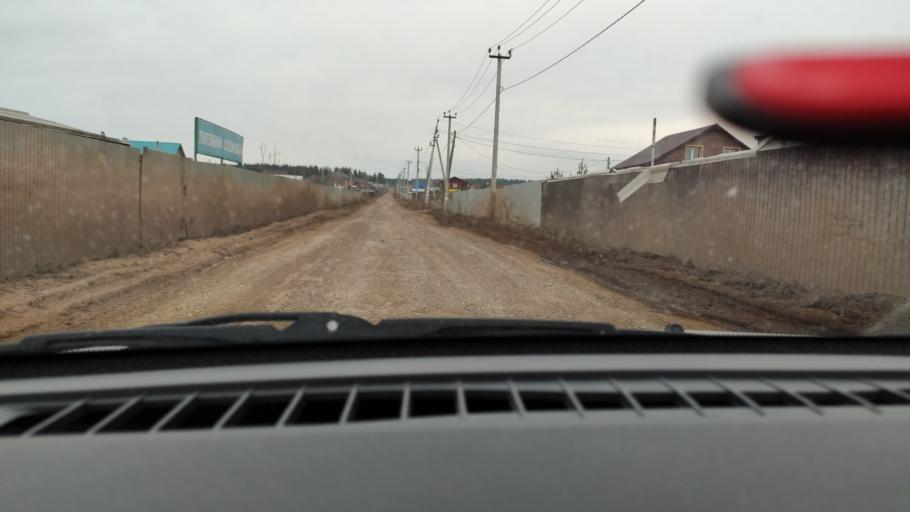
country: RU
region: Perm
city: Kultayevo
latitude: 57.8988
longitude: 55.9962
